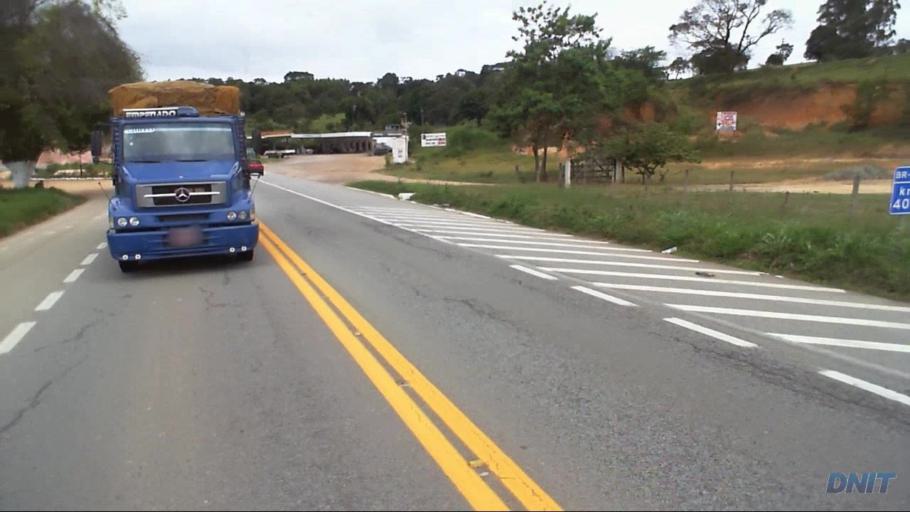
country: BR
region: Minas Gerais
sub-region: Caete
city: Caete
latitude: -19.7395
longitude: -43.5566
